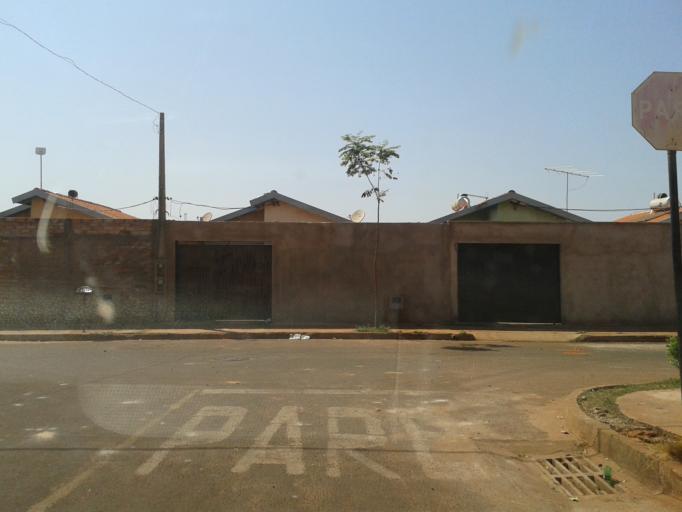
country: BR
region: Minas Gerais
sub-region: Ituiutaba
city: Ituiutaba
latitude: -19.0164
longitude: -49.4529
